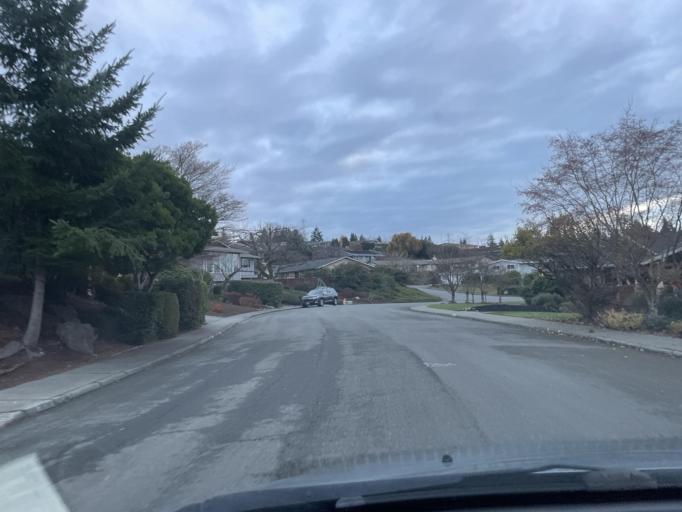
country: US
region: Washington
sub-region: King County
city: Newport
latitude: 47.5937
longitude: -122.1786
